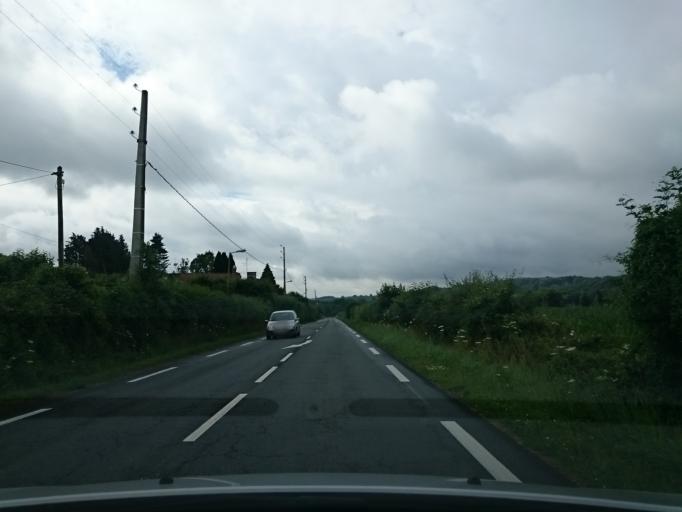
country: FR
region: Lower Normandy
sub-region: Departement du Calvados
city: Beuvillers
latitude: 49.1171
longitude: 0.2836
